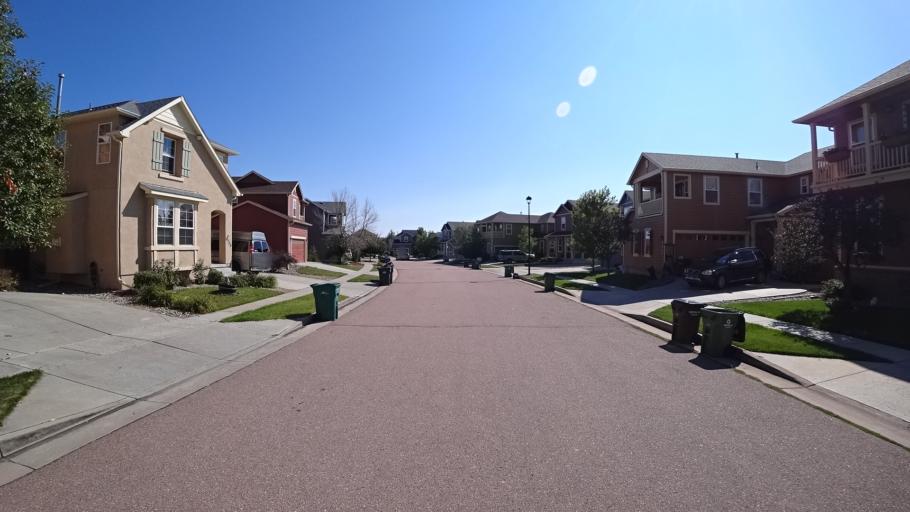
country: US
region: Colorado
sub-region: El Paso County
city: Cimarron Hills
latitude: 38.9273
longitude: -104.7016
